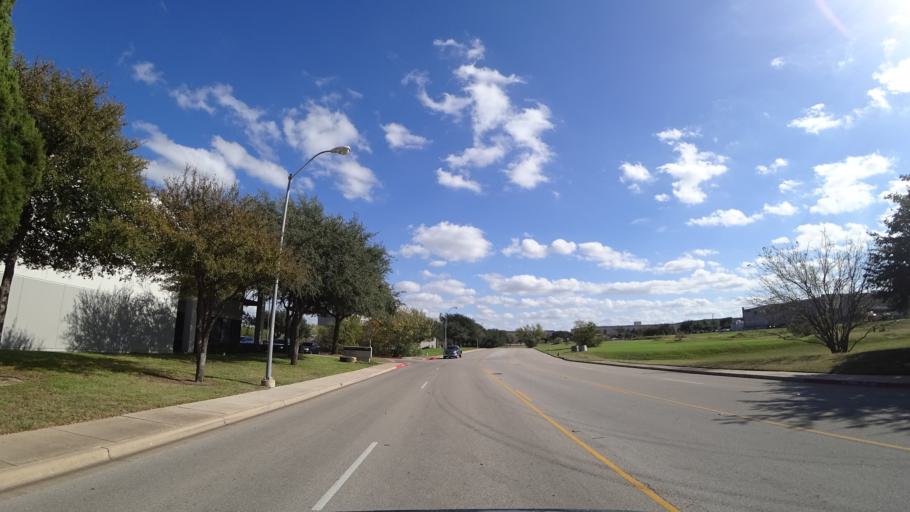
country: US
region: Texas
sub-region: Travis County
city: Wells Branch
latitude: 30.4752
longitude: -97.6758
